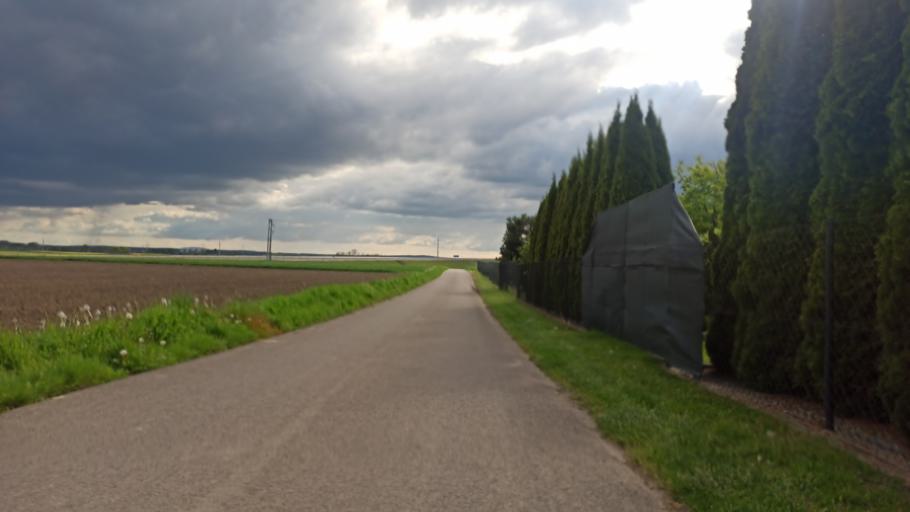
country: PL
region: Subcarpathian Voivodeship
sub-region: Powiat jaroslawski
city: Sosnica
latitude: 49.9169
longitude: 22.8590
